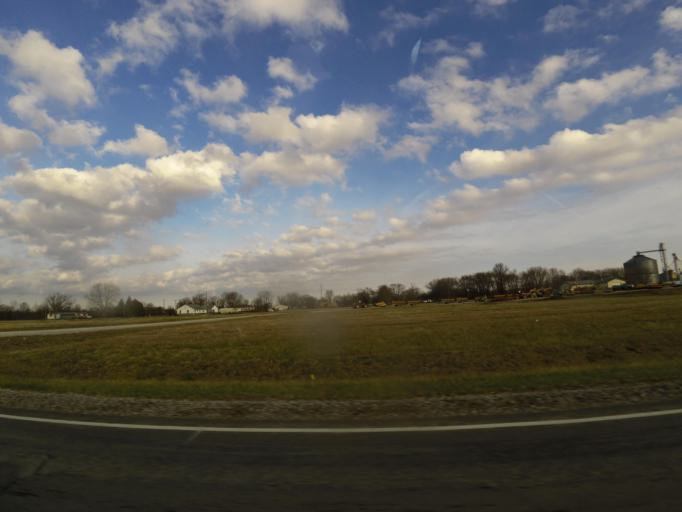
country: US
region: Illinois
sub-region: Bond County
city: Greenville
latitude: 38.9185
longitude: -89.2741
